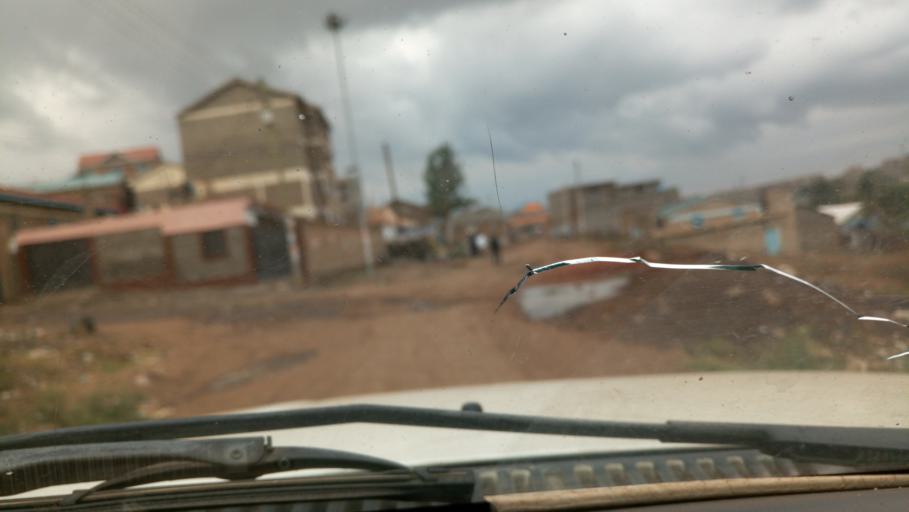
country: KE
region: Nairobi Area
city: Pumwani
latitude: -1.2427
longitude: 36.8954
